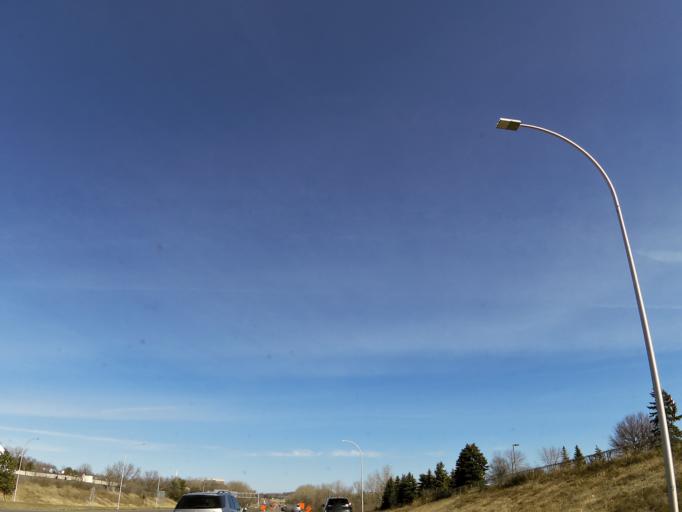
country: US
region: Minnesota
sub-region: Hennepin County
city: Eden Prairie
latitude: 44.8693
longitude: -93.4163
